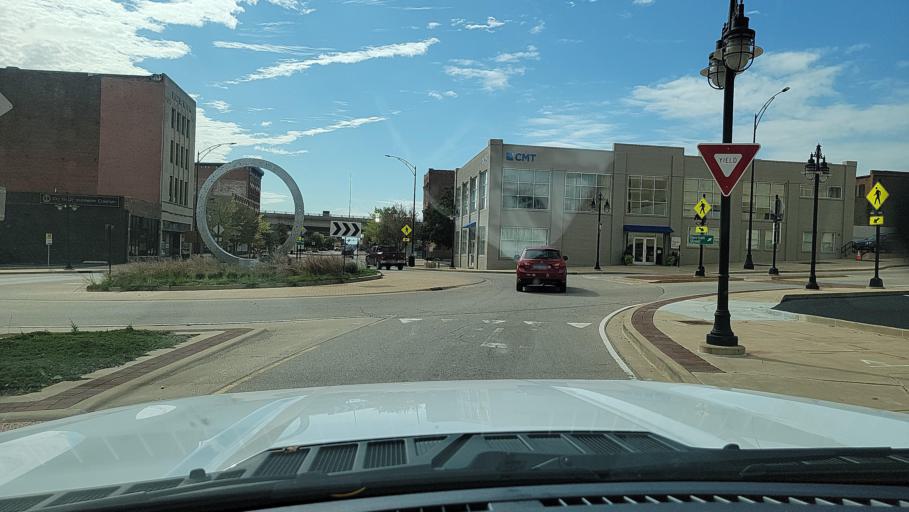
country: US
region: Illinois
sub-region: Peoria County
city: Peoria
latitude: 40.6887
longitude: -89.5921
